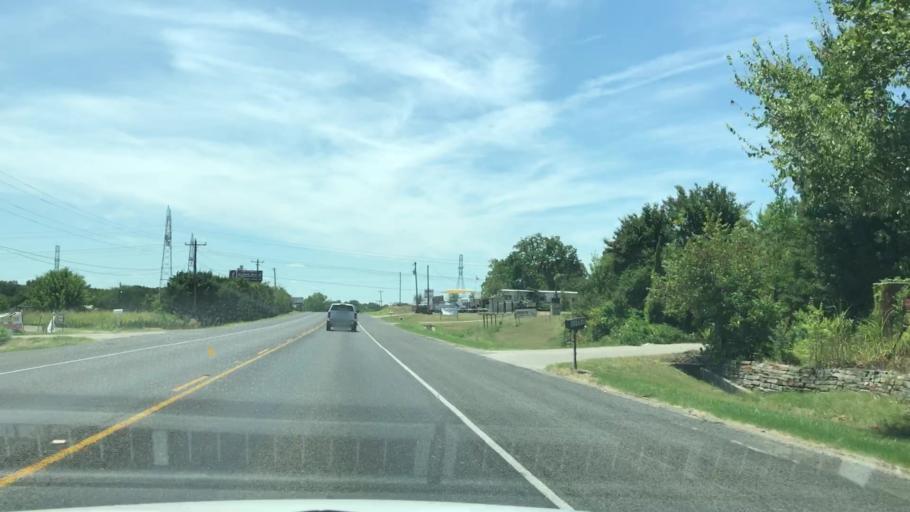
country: US
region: Texas
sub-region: Collin County
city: Lavon
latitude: 33.0074
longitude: -96.4605
